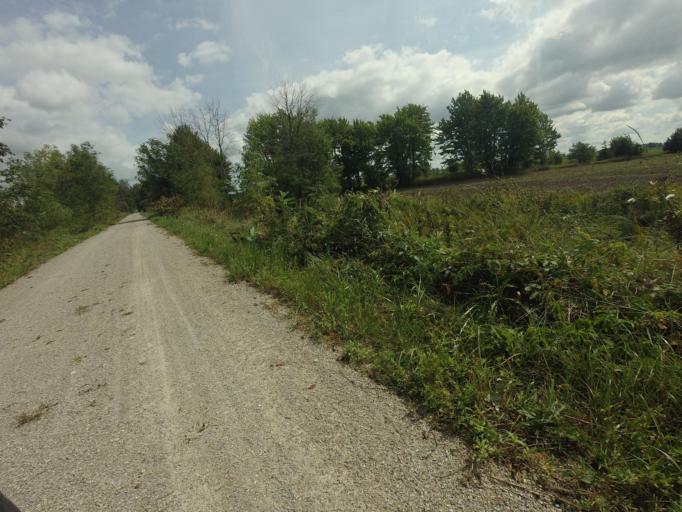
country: CA
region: Ontario
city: North Perth
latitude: 43.5656
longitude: -80.9621
